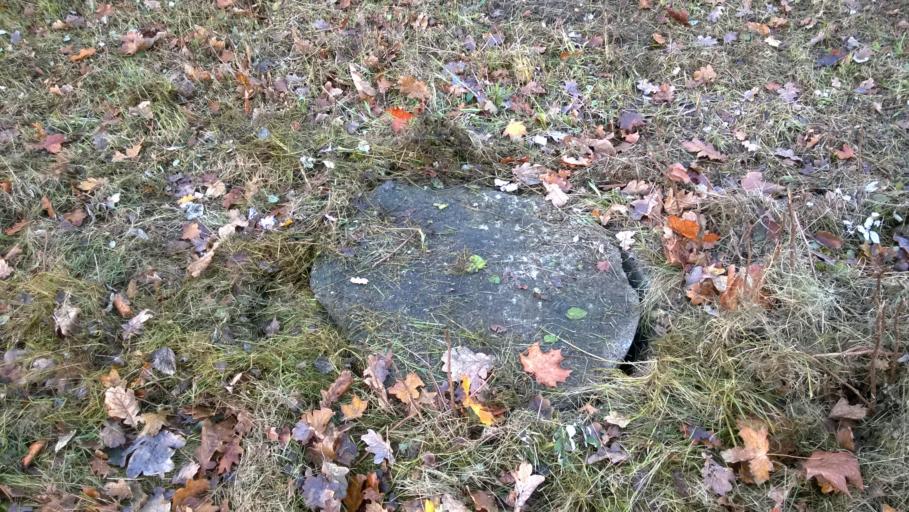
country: DK
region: North Denmark
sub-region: Morso Kommune
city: Nykobing Mors
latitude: 56.7514
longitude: 8.8778
